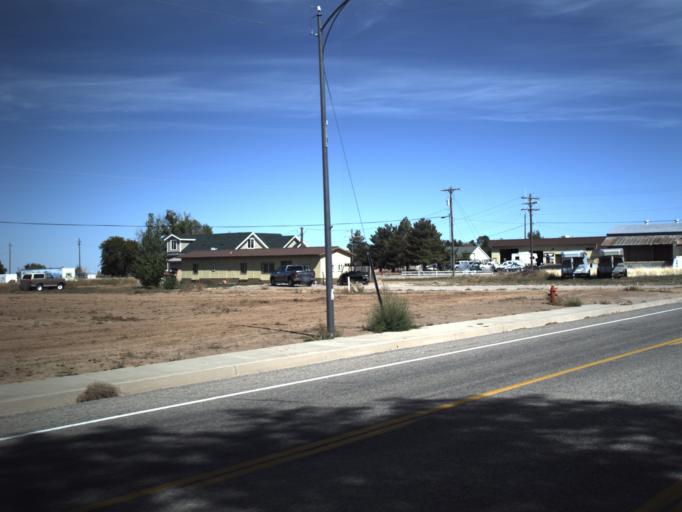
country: US
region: Utah
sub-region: Washington County
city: Enterprise
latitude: 37.5736
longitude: -113.7130
